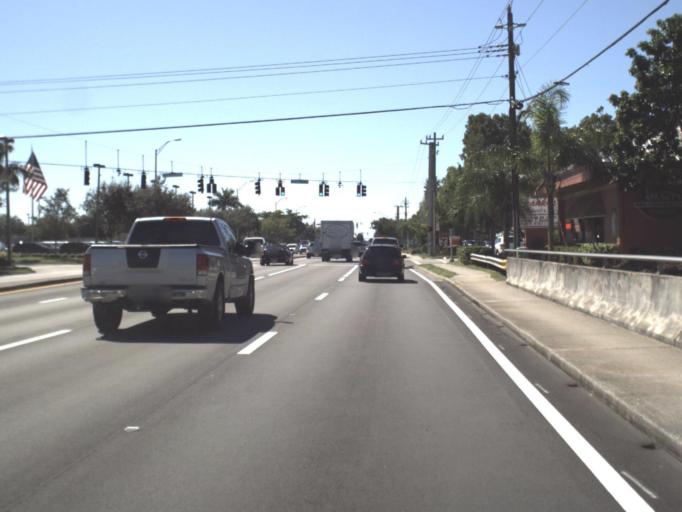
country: US
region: Florida
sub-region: Collier County
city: Naples
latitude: 26.1681
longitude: -81.7672
